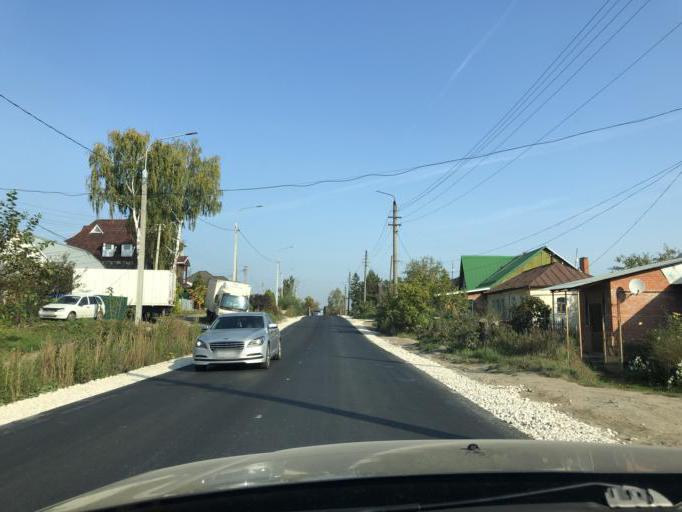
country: RU
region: Tula
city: Leninskiy
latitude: 54.2913
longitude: 37.4643
